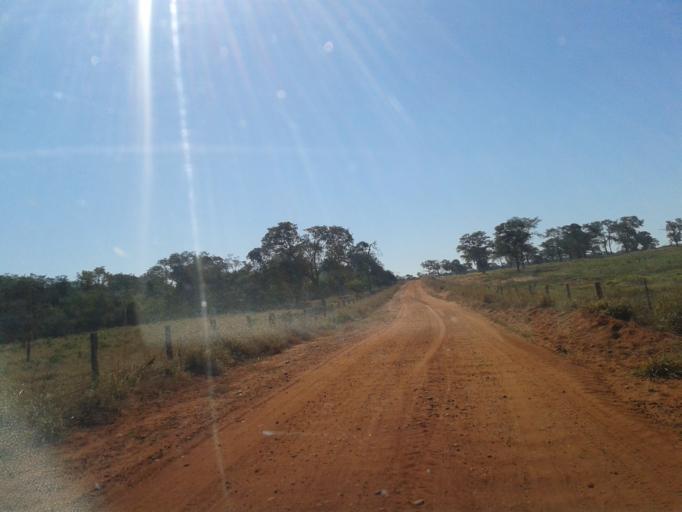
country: BR
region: Minas Gerais
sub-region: Santa Vitoria
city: Santa Vitoria
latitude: -19.0351
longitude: -50.3646
